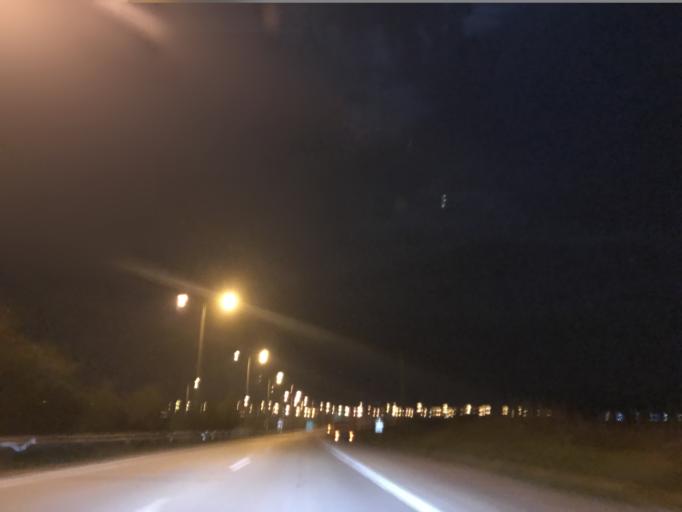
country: TR
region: Hatay
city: Mahmutlar
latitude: 36.9649
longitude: 36.1024
